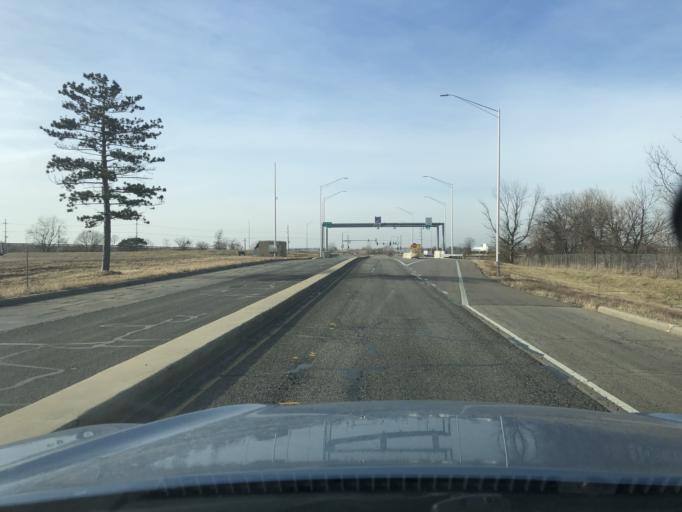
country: US
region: Illinois
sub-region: Boone County
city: Belvidere
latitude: 42.2356
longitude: -88.8158
